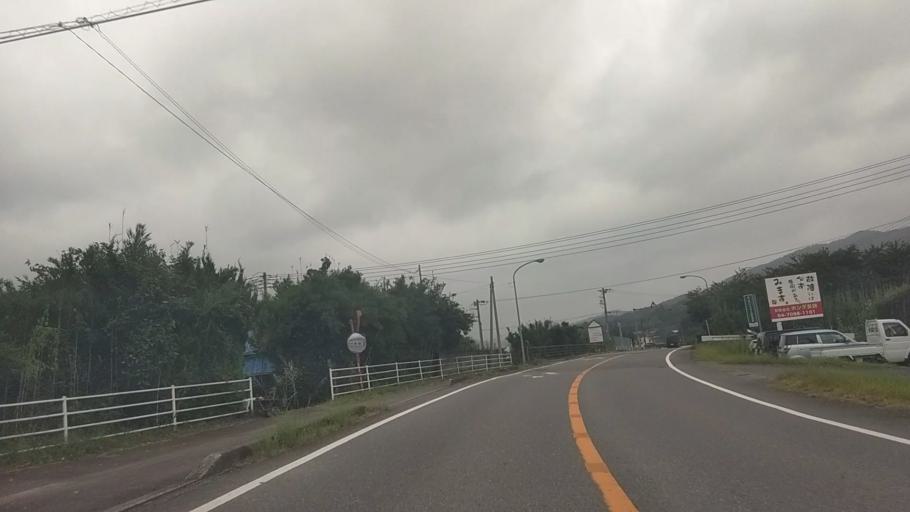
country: JP
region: Chiba
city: Kawaguchi
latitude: 35.1369
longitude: 139.9906
